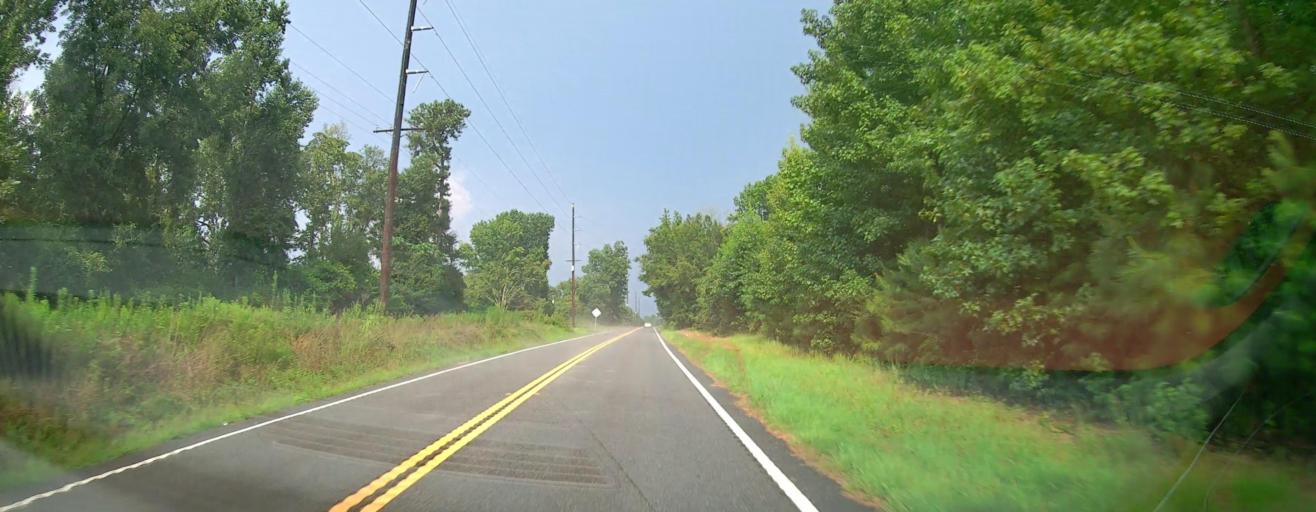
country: US
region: Georgia
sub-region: Twiggs County
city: Jeffersonville
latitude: 32.6032
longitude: -83.2976
